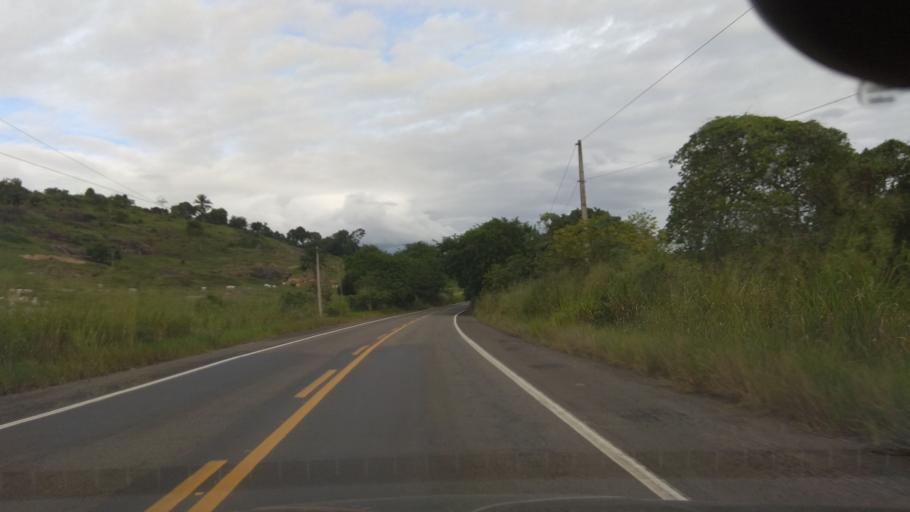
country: BR
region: Bahia
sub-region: Ipiau
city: Ipiau
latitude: -14.1830
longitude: -39.6622
